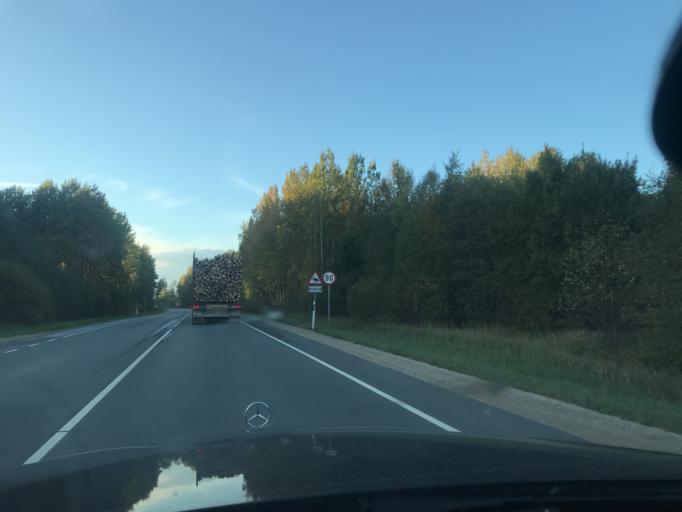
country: EE
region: Vorumaa
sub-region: Voru linn
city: Voru
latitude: 57.8617
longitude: 26.9678
